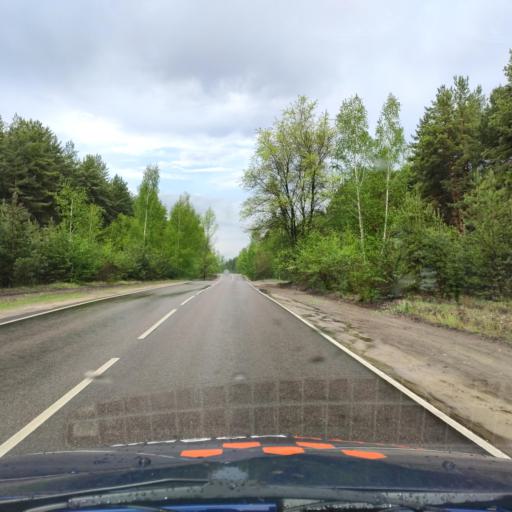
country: RU
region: Voronezj
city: Maslovka
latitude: 51.5474
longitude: 39.2144
